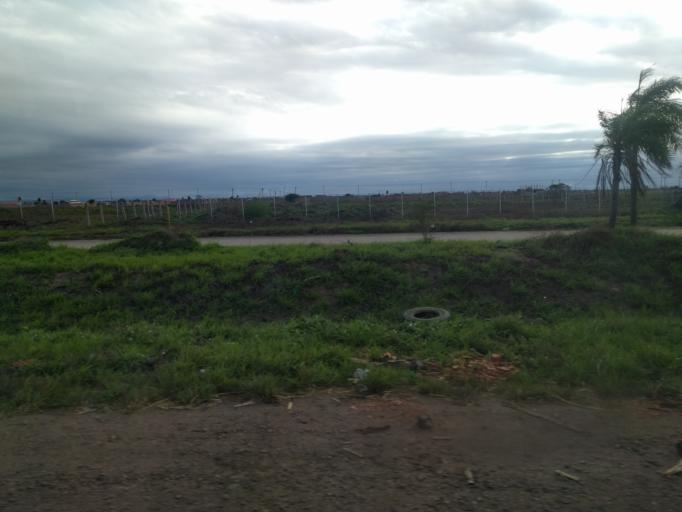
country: BO
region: Santa Cruz
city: La Belgica
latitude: -17.5964
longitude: -63.1588
